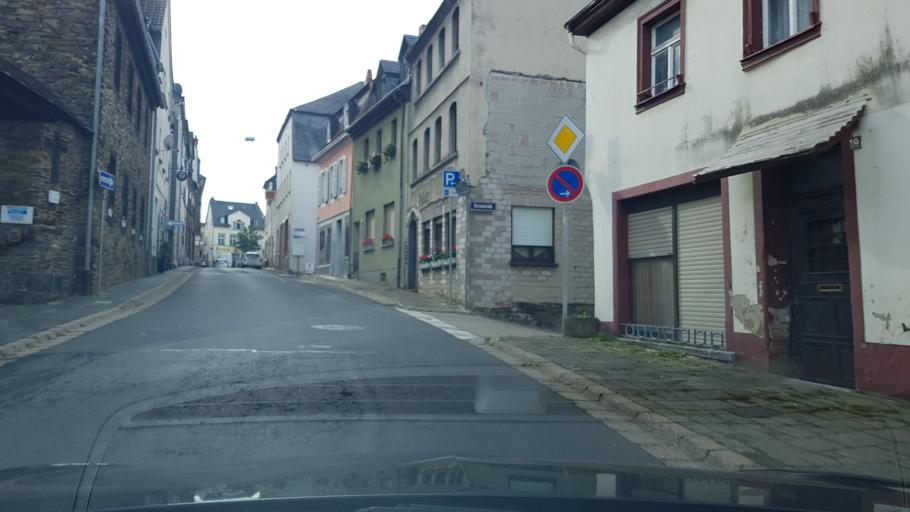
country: DE
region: Rheinland-Pfalz
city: Munstermaifeld
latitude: 50.2476
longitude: 7.3607
